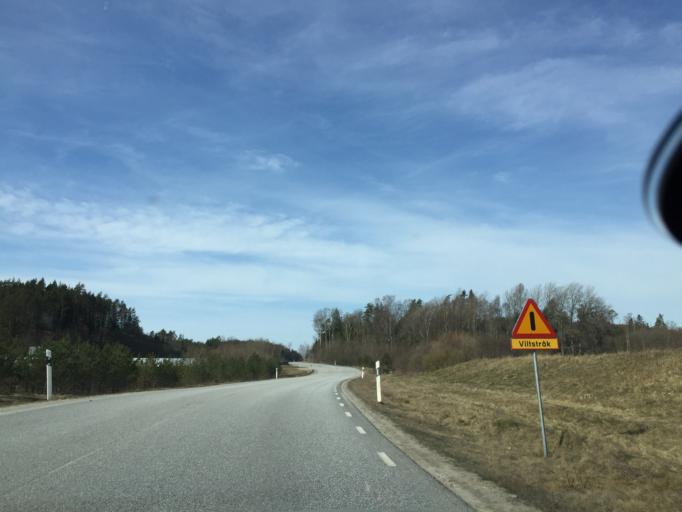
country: SE
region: Vaestra Goetaland
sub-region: Uddevalla Kommun
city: Uddevalla
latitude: 58.3635
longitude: 11.8039
